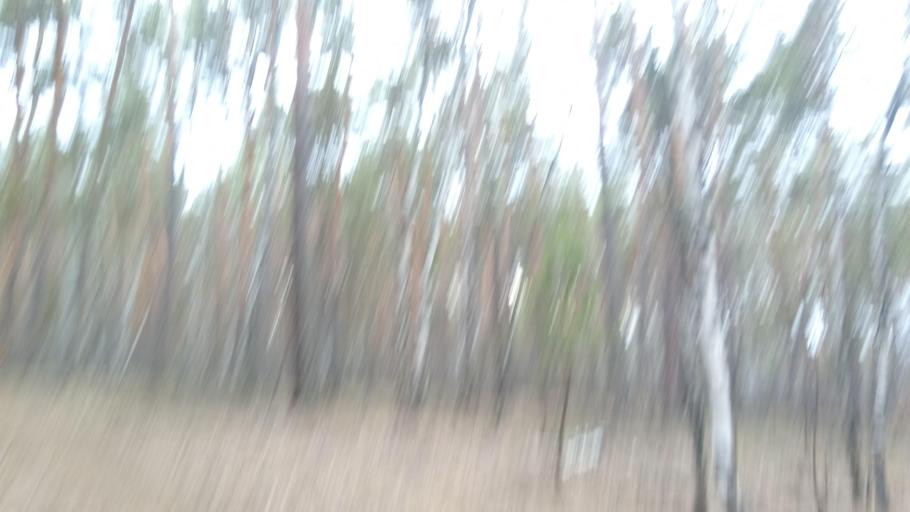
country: RU
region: Chelyabinsk
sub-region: Gorod Chelyabinsk
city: Chelyabinsk
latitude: 55.1377
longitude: 61.3395
